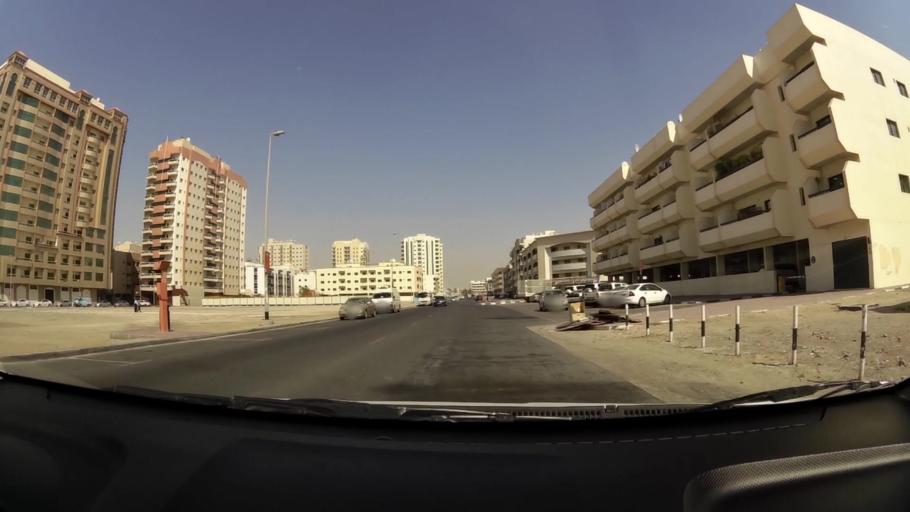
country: AE
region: Ash Shariqah
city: Sharjah
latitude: 25.2766
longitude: 55.3769
